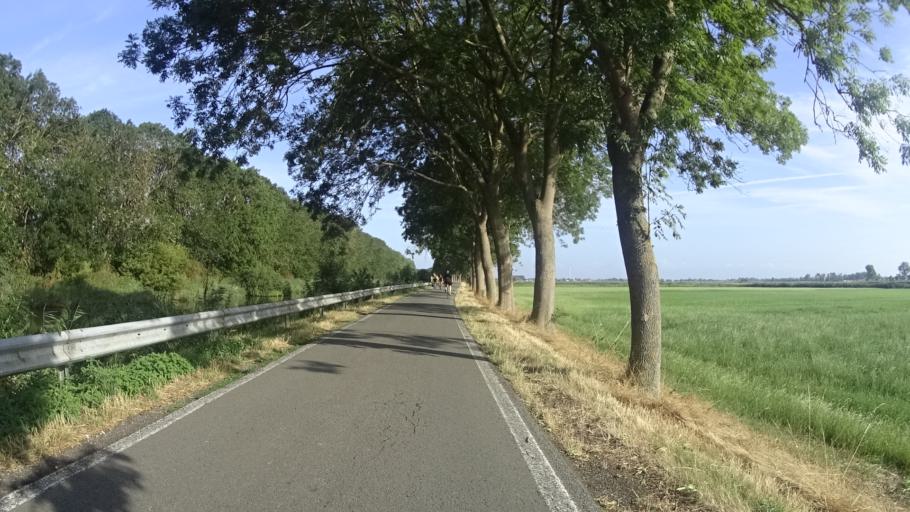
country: BE
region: Flanders
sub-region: Provincie West-Vlaanderen
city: Diksmuide
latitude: 50.9660
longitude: 2.8177
